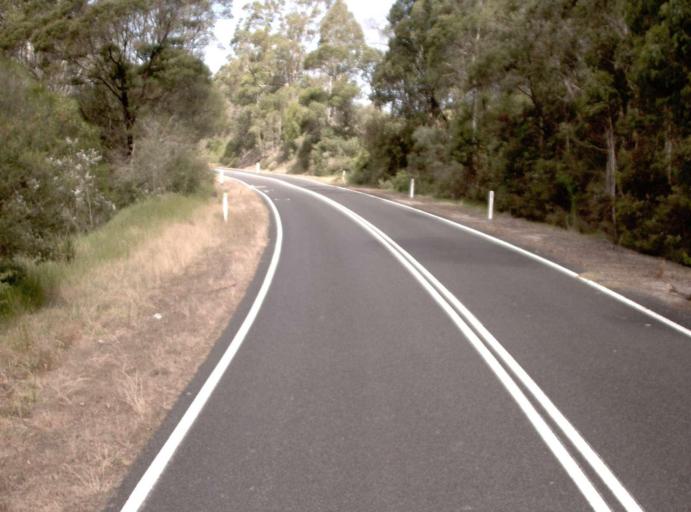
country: AU
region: New South Wales
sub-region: Bega Valley
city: Eden
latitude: -37.4803
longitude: 149.6201
